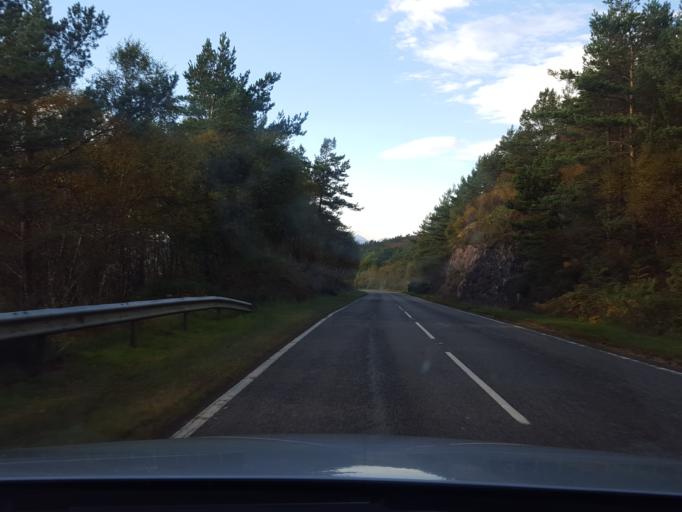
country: GB
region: Scotland
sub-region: Highland
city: Portree
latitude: 57.2825
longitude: -5.6661
